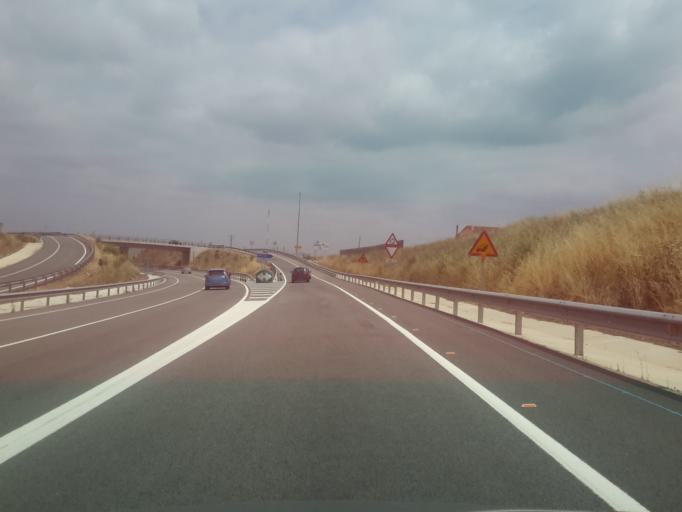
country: ES
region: Catalonia
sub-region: Provincia de Barcelona
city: Vilafranca del Penedes
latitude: 41.3479
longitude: 1.7218
